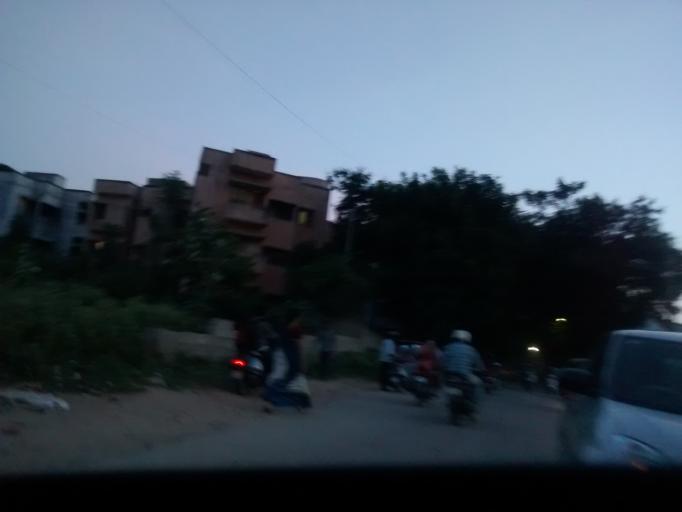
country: IN
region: Karnataka
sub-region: Bangalore Urban
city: Bangalore
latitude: 12.9744
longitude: 77.6698
